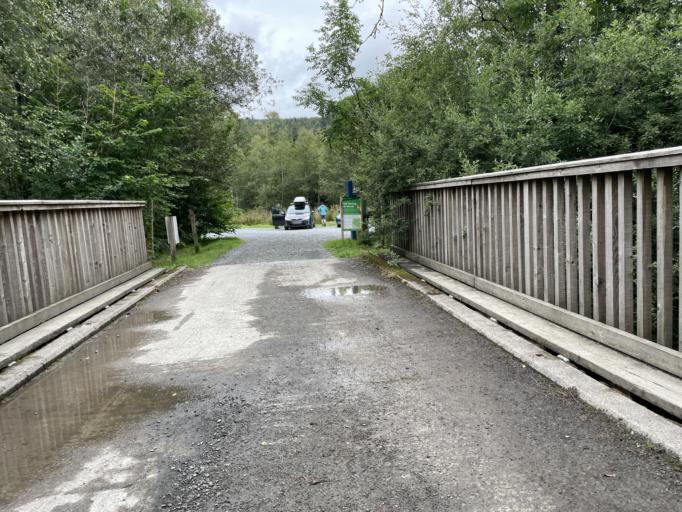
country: GB
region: Scotland
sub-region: Dumfries and Galloway
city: Newton Stewart
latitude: 55.0799
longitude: -4.5124
